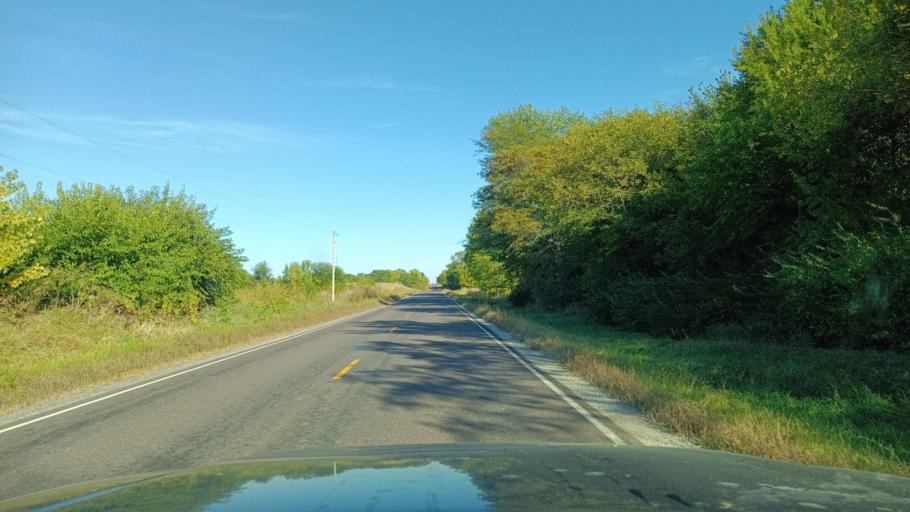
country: US
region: Illinois
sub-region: McLean County
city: Heyworth
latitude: 40.2315
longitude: -89.0065
